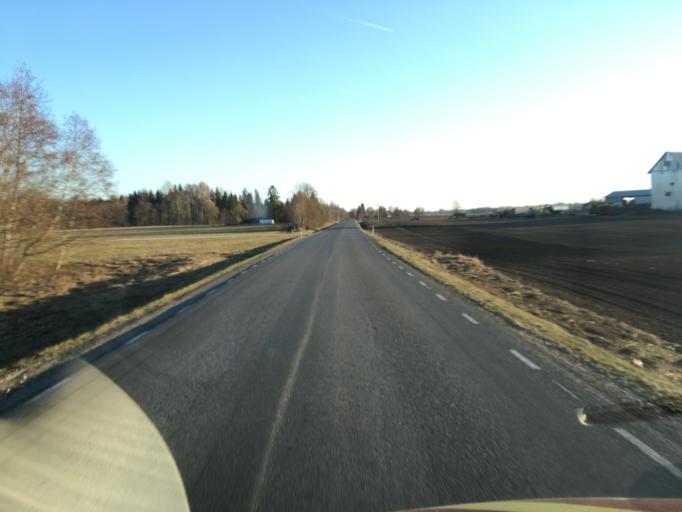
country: EE
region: Raplamaa
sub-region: Kehtna vald
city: Kehtna
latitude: 59.0508
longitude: 24.9491
